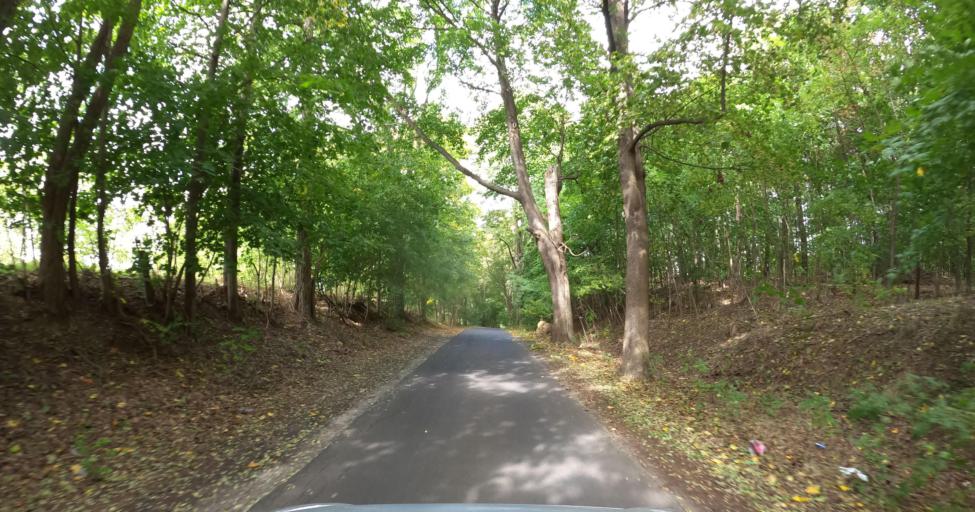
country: PL
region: Lubusz
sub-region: Powiat zielonogorski
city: Zabor
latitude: 51.9553
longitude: 15.6894
